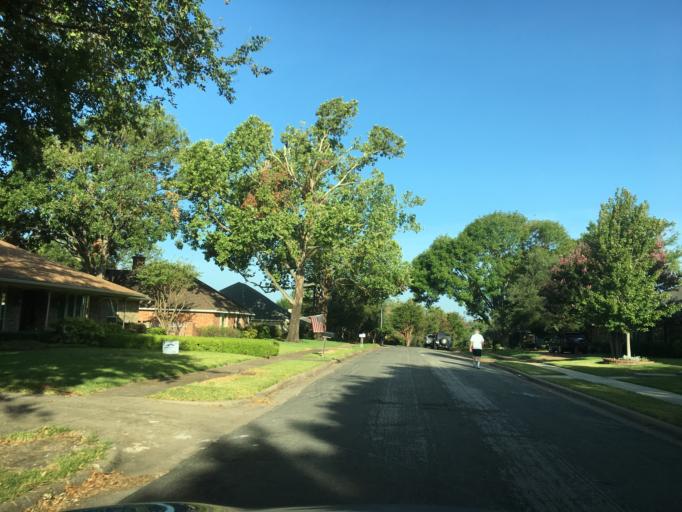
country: US
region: Texas
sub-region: Dallas County
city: Richardson
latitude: 32.8867
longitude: -96.7394
